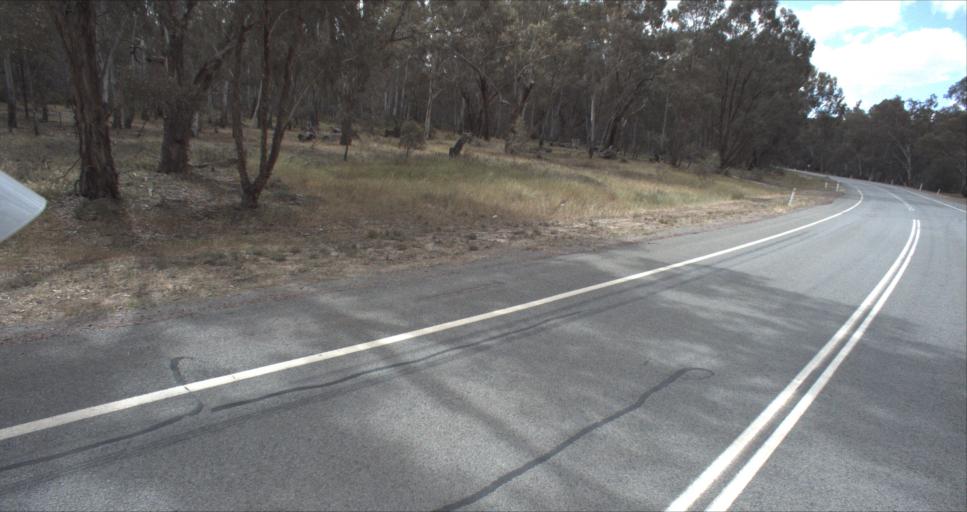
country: AU
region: New South Wales
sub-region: Leeton
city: Leeton
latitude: -34.6375
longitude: 146.3751
